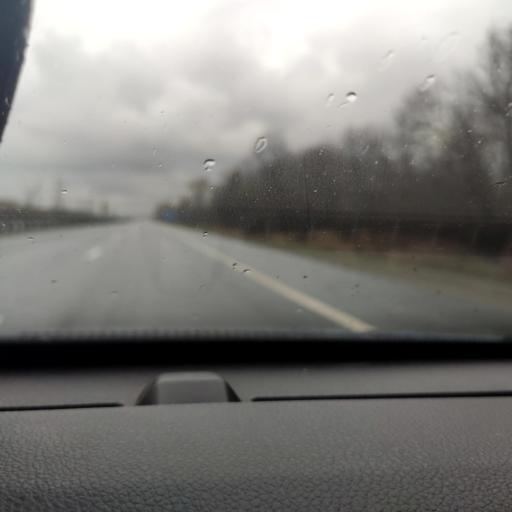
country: RU
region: Samara
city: Pribrezhnyy
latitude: 53.5170
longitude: 49.8166
